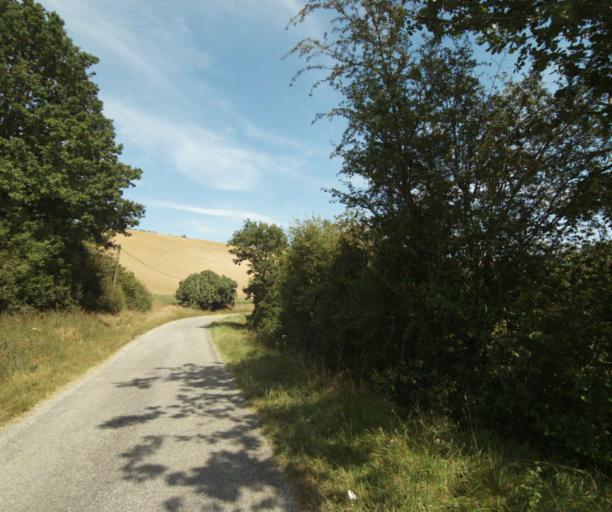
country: FR
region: Midi-Pyrenees
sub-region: Departement de l'Ariege
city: Lezat-sur-Leze
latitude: 43.2486
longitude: 1.4051
